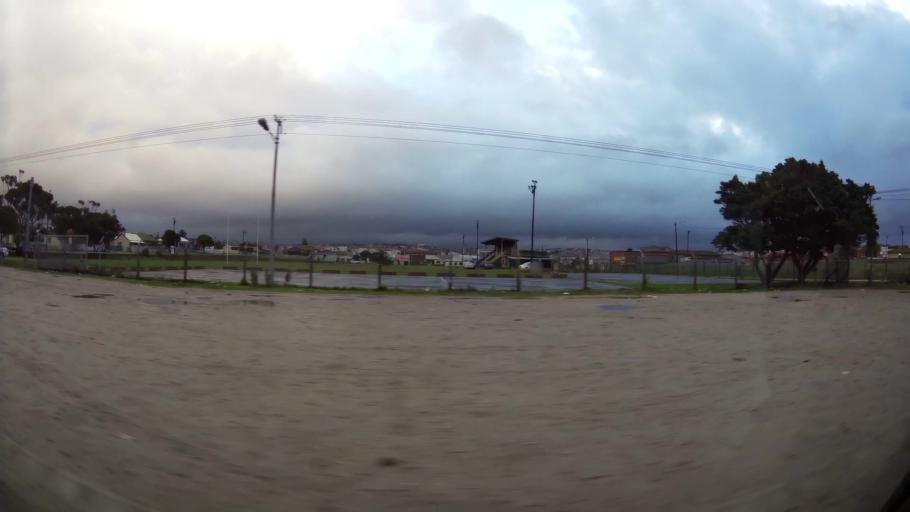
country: ZA
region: Eastern Cape
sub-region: Nelson Mandela Bay Metropolitan Municipality
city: Port Elizabeth
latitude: -33.9274
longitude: 25.5972
